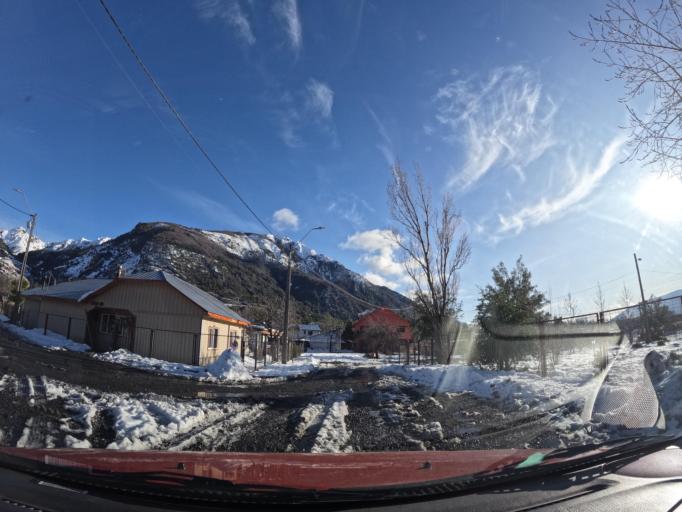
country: CL
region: Biobio
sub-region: Provincia de Nuble
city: Coihueco
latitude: -37.3698
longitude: -71.4874
